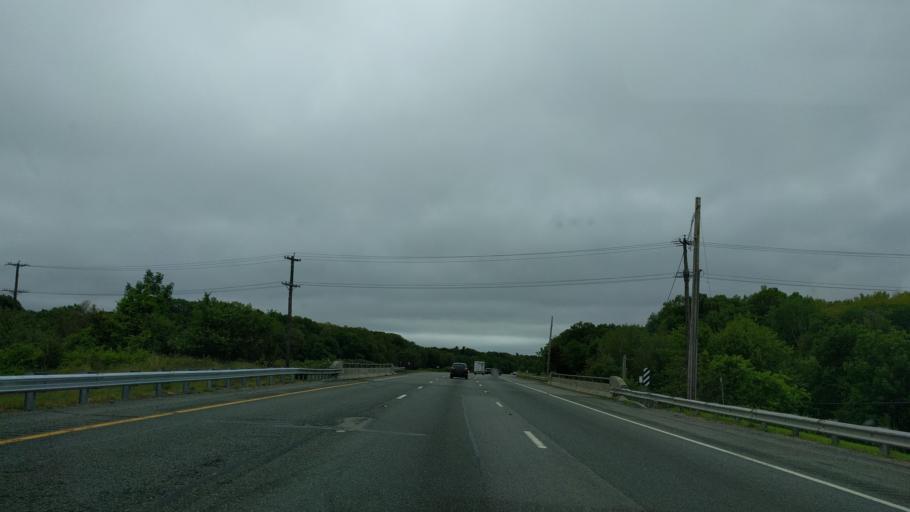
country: US
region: Rhode Island
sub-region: Providence County
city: Johnston
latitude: 41.8503
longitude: -71.5115
